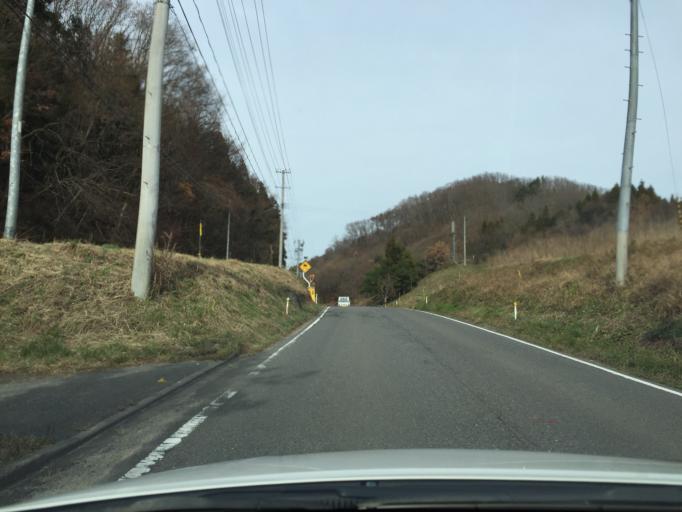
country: JP
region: Fukushima
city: Funehikimachi-funehiki
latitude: 37.3721
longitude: 140.6006
